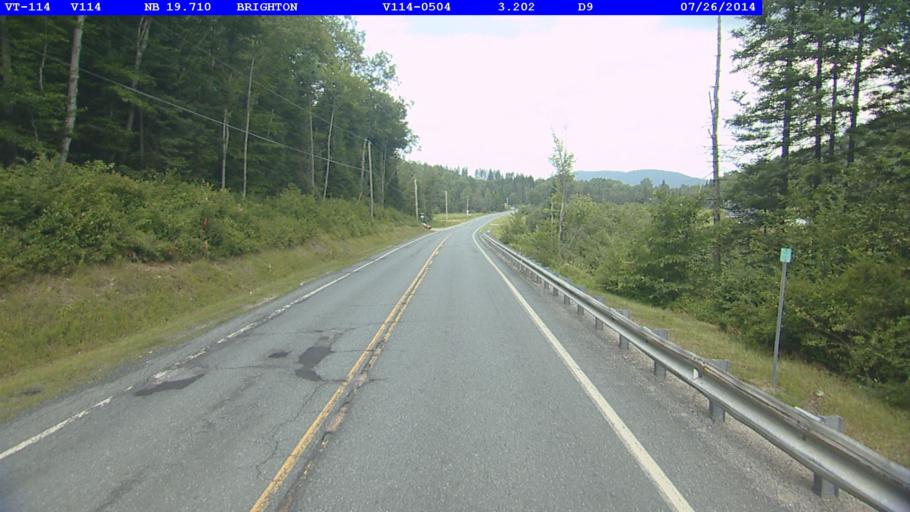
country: US
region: Vermont
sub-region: Caledonia County
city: Lyndonville
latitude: 44.7801
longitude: -71.9098
